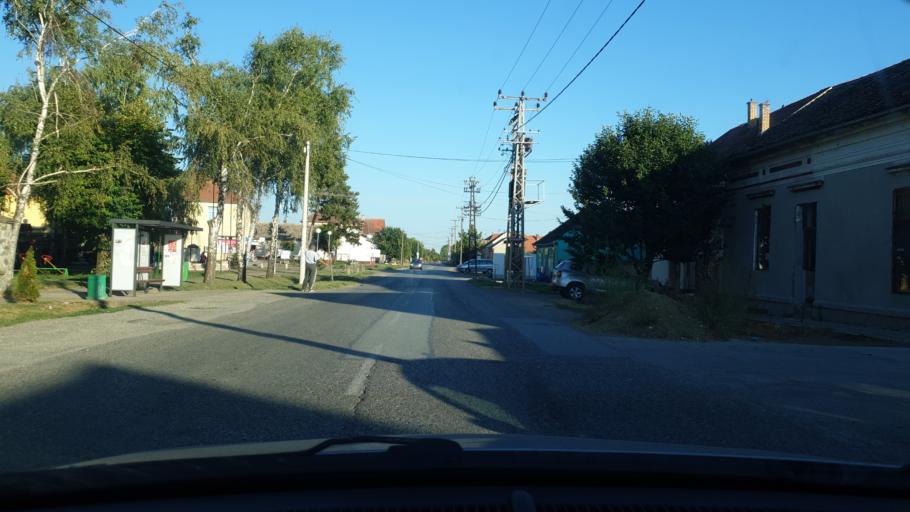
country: RS
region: Autonomna Pokrajina Vojvodina
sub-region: Sremski Okrug
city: Ruma
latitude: 44.9777
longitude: 19.8831
